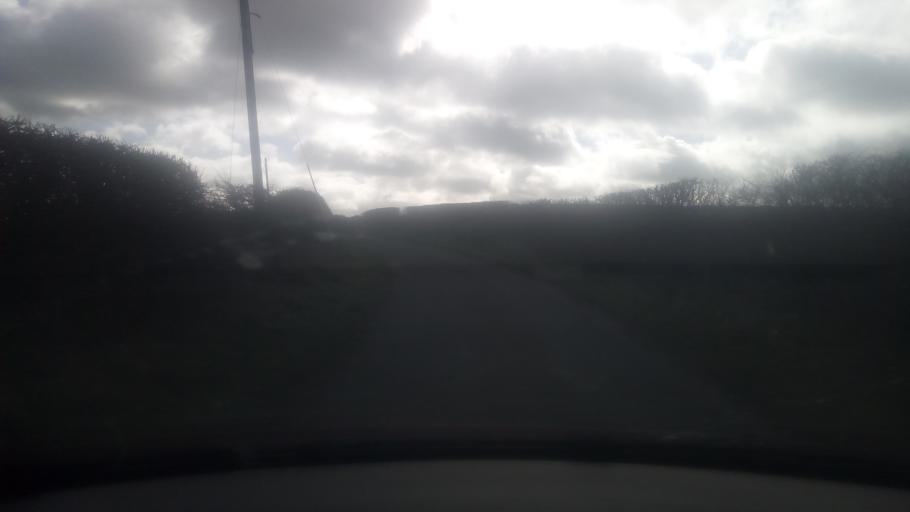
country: GB
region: Scotland
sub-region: The Scottish Borders
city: Saint Boswells
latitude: 55.5227
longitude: -2.6556
